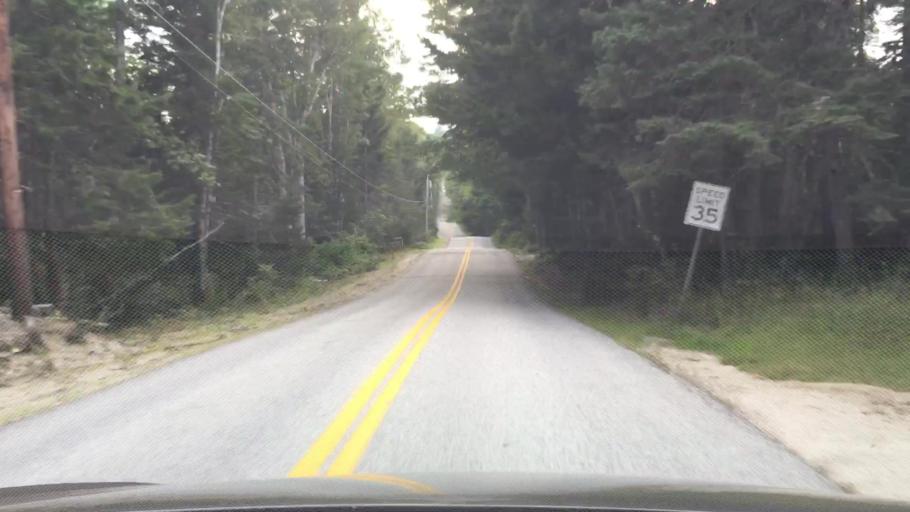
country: US
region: Maine
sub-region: Hancock County
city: Penobscot
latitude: 44.4474
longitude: -68.6170
